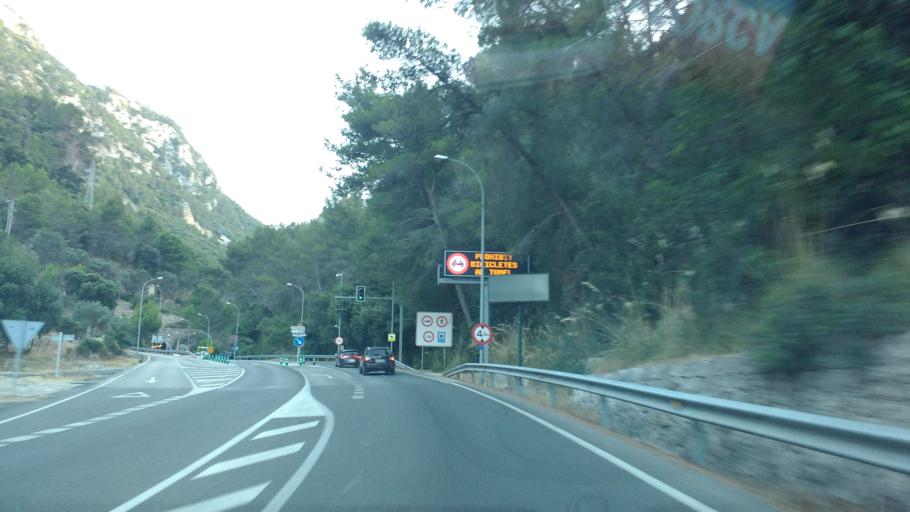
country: ES
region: Balearic Islands
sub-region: Illes Balears
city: Soller
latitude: 39.7467
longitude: 2.6980
